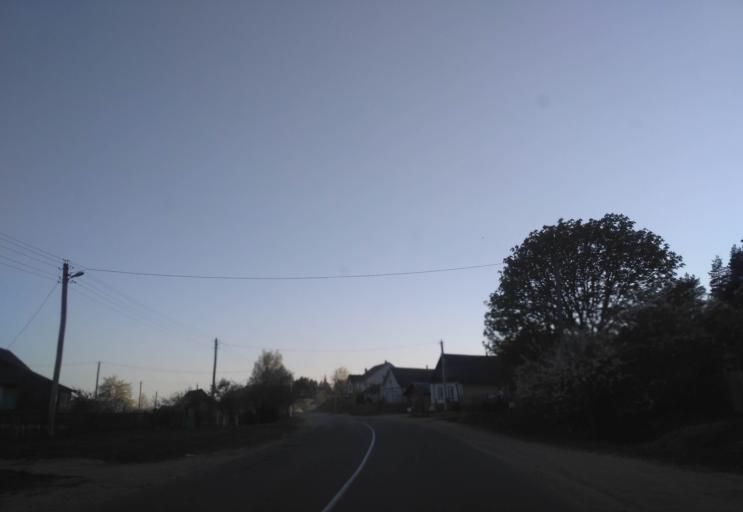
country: BY
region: Minsk
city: Radashkovichy
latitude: 54.1540
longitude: 27.2207
